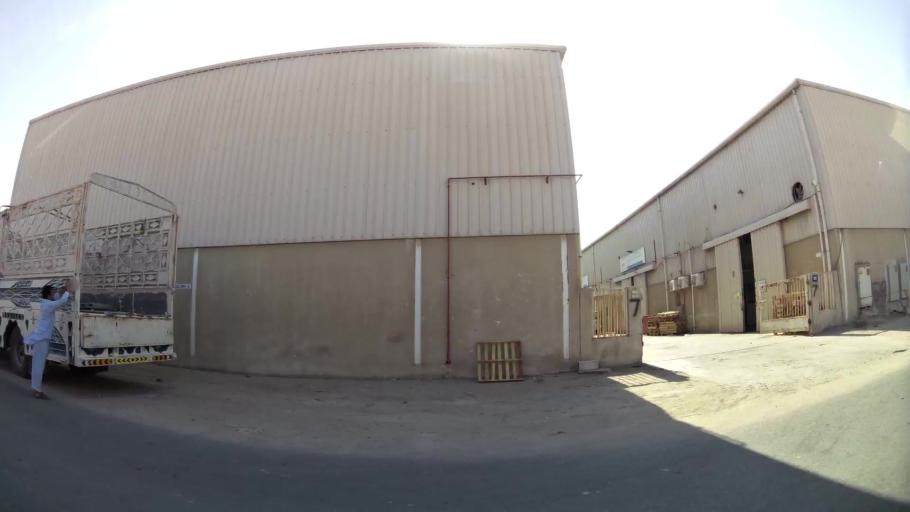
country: AE
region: Dubai
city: Dubai
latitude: 24.9893
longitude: 55.0984
